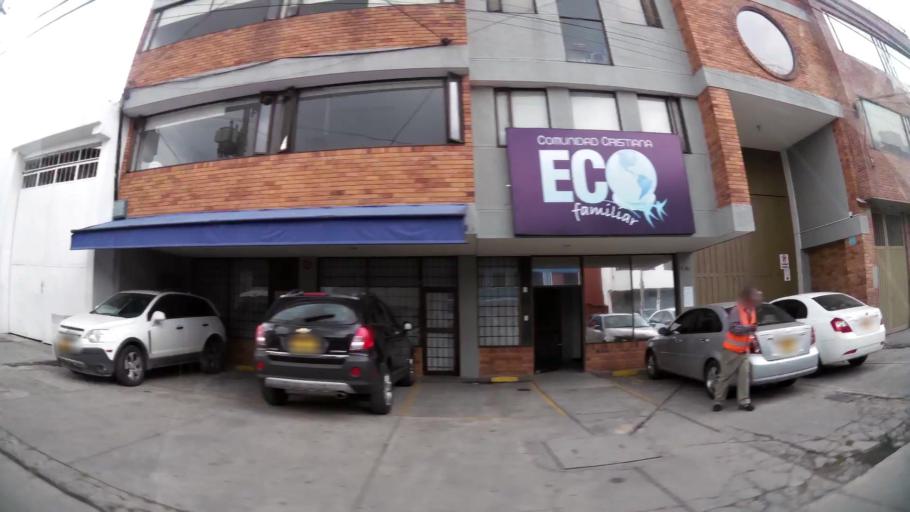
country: CO
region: Cundinamarca
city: La Calera
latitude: 4.7464
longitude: -74.0455
